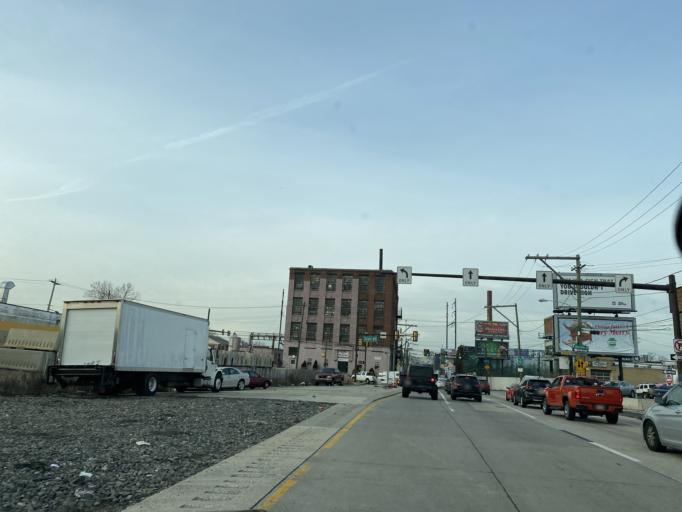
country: US
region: New Jersey
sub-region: Burlington County
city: Palmyra
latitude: 40.0250
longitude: -75.0312
